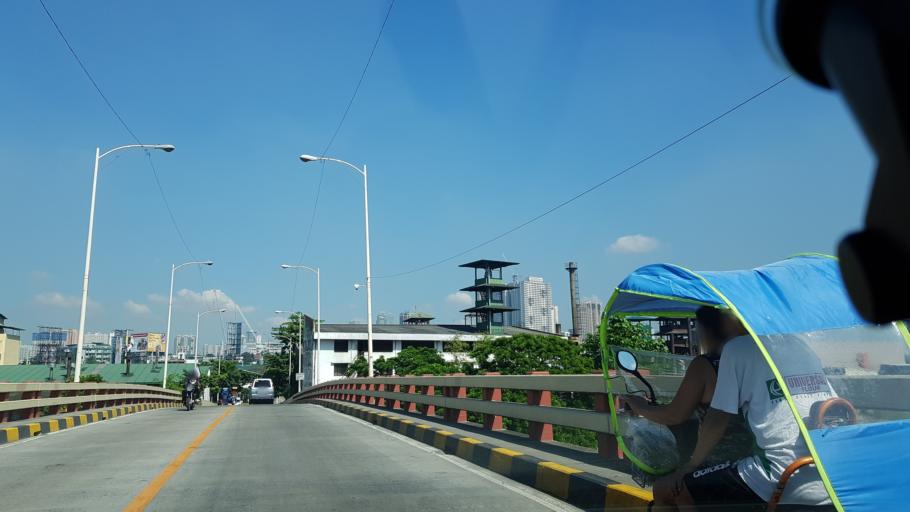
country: PH
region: Calabarzon
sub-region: Province of Rizal
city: Pateros
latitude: 14.5599
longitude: 121.0724
